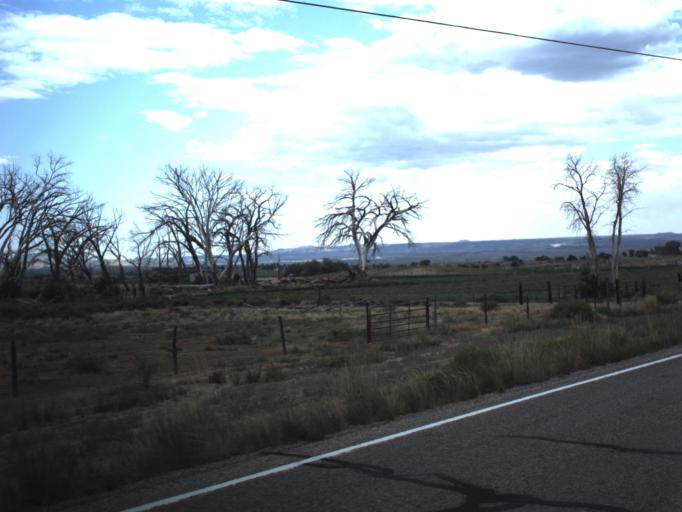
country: US
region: Utah
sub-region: Emery County
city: Huntington
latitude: 39.4081
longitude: -110.8529
